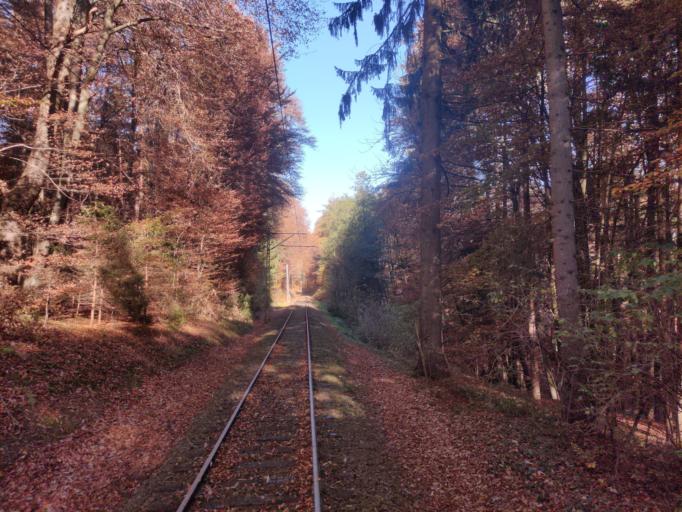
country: AT
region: Styria
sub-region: Politischer Bezirk Suedoststeiermark
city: Maierdorf
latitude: 46.9180
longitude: 15.8423
